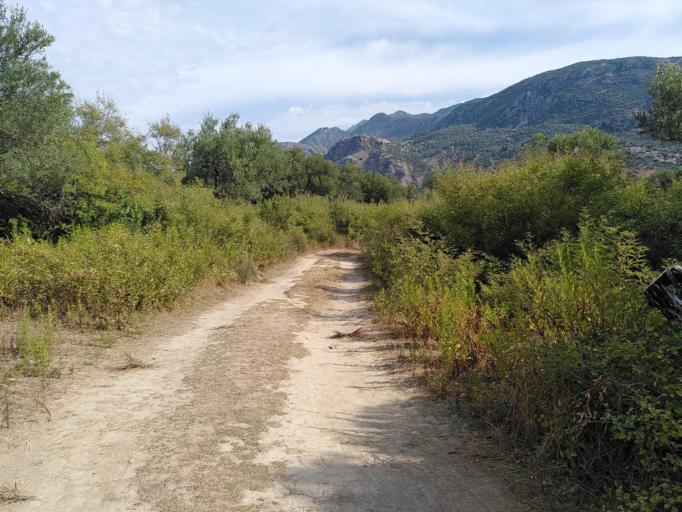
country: AL
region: Vlore
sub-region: Rrethi i Vlores
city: Himare
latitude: 40.0534
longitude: 19.8190
